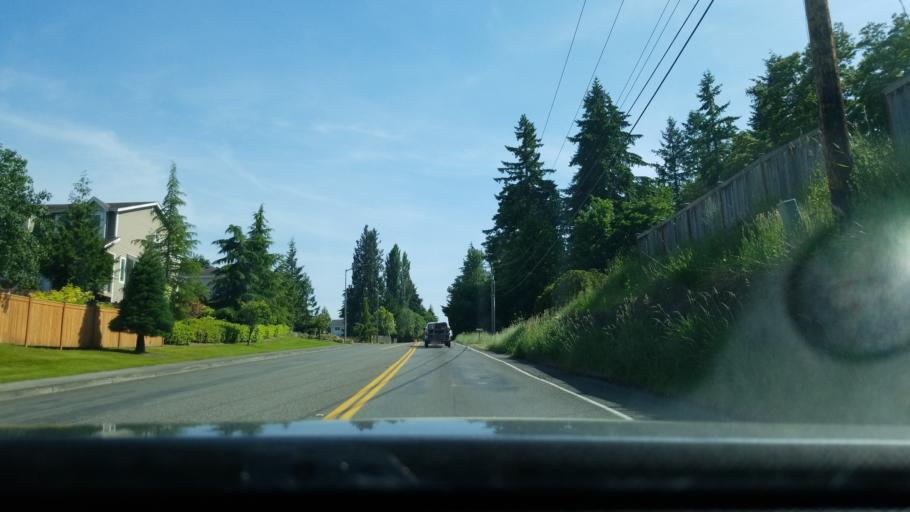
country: US
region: Washington
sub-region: Pierce County
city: Puyallup
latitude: 47.1676
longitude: -122.3043
